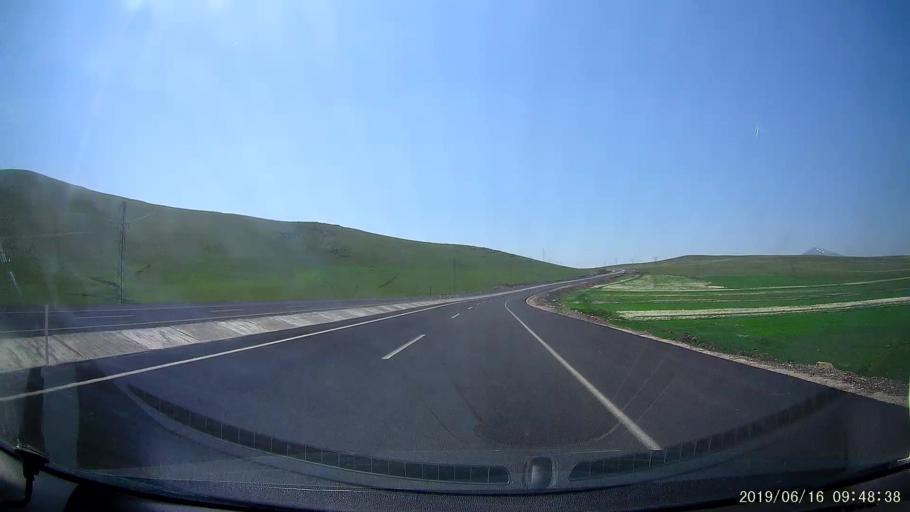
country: TR
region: Kars
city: Digor
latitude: 40.4315
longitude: 43.3546
